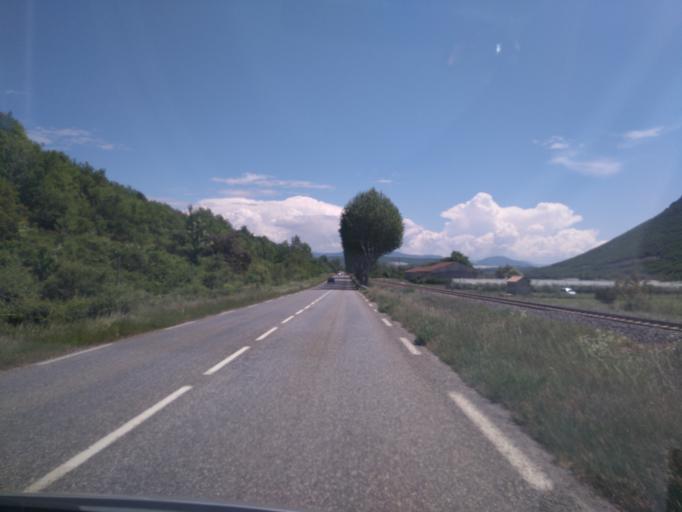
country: FR
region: Provence-Alpes-Cote d'Azur
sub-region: Departement des Hautes-Alpes
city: Laragne-Monteglin
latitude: 44.3213
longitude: 5.8035
